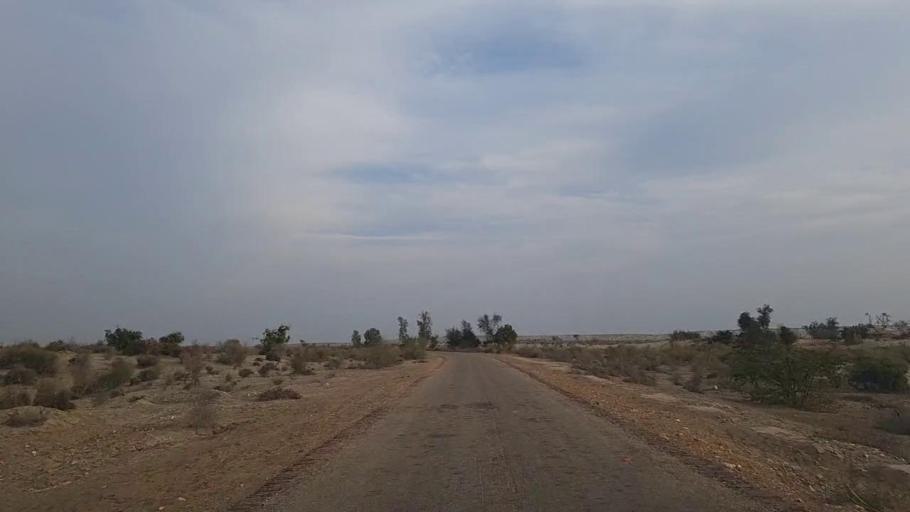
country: PK
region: Sindh
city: Daur
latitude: 26.4952
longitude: 68.5271
